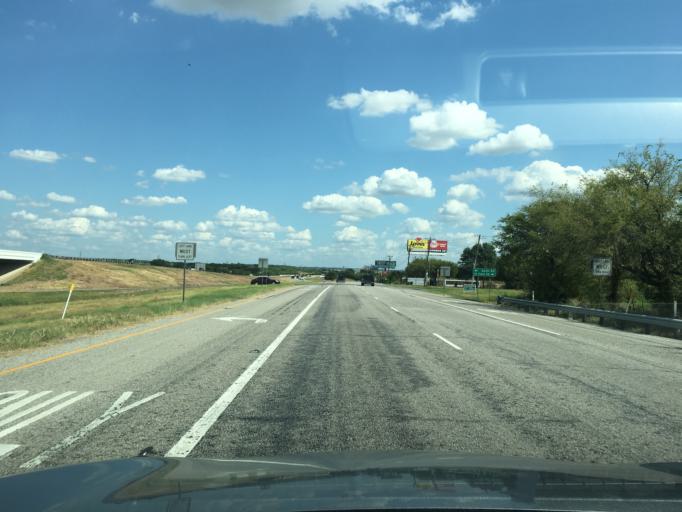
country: US
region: Texas
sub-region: Tarrant County
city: Mansfield
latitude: 32.5167
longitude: -97.0745
